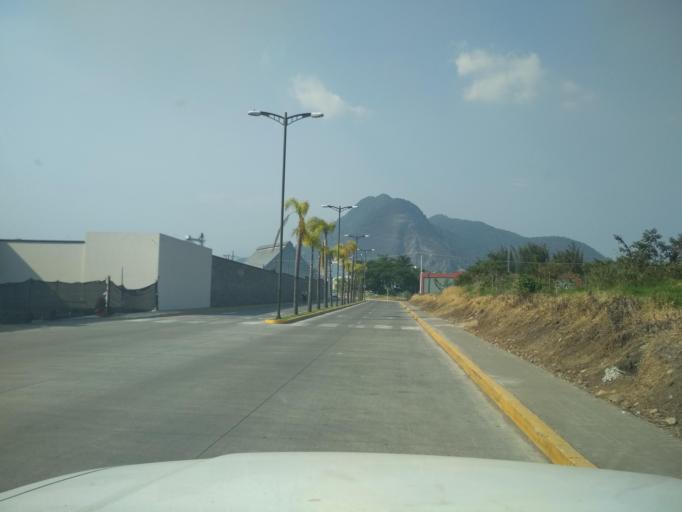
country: MX
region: Veracruz
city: Orizaba
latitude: 18.8421
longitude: -97.0874
